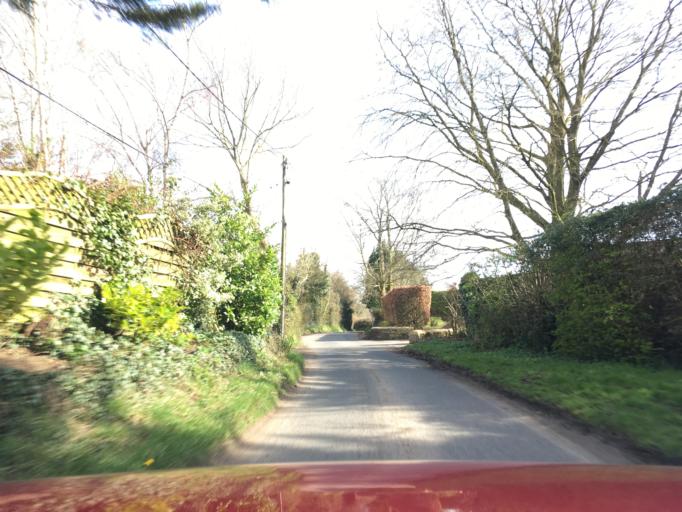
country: GB
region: England
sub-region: Wiltshire
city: Chippenham
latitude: 51.4925
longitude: -2.1088
